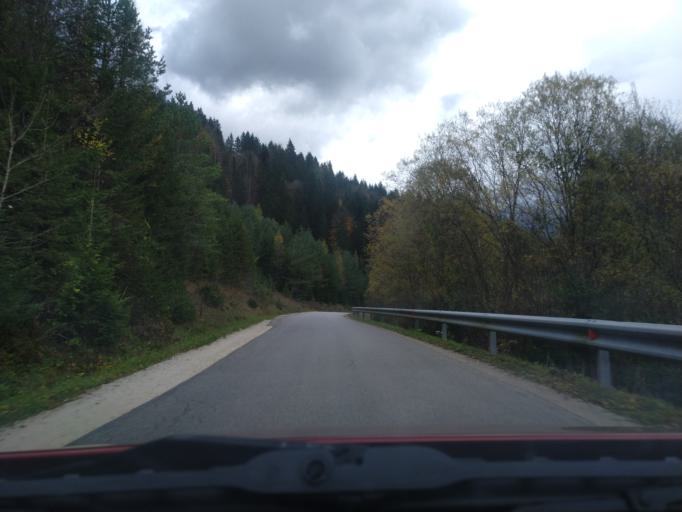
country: SI
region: Luce
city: Luce
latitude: 46.3458
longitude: 14.7300
